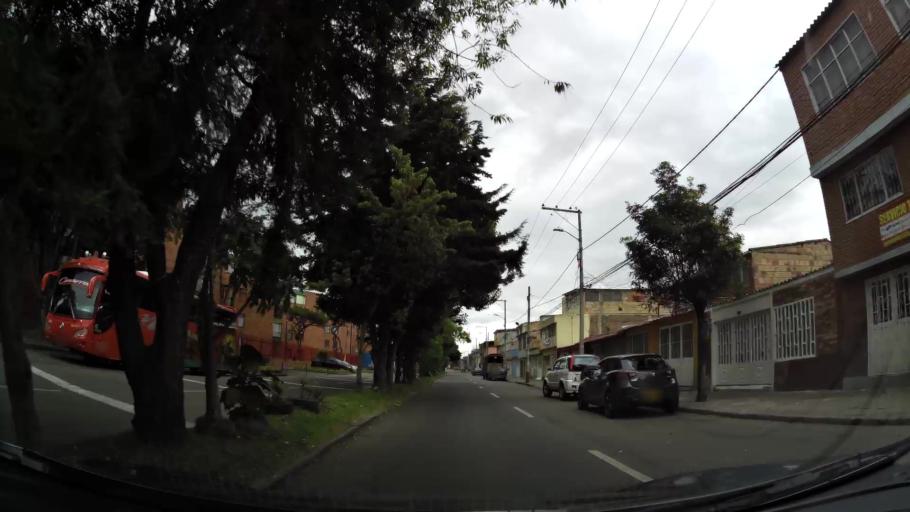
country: CO
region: Bogota D.C.
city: Barrio San Luis
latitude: 4.7032
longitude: -74.1071
